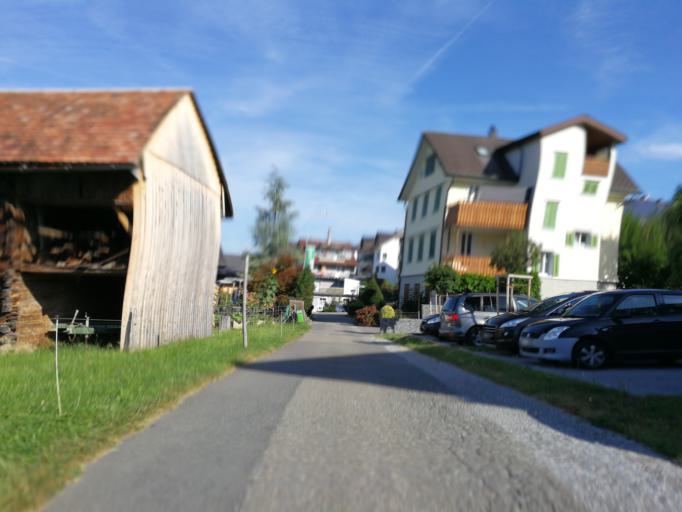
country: CH
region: Saint Gallen
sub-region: Wahlkreis See-Gaster
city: Gommiswald
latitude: 47.2297
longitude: 9.0259
